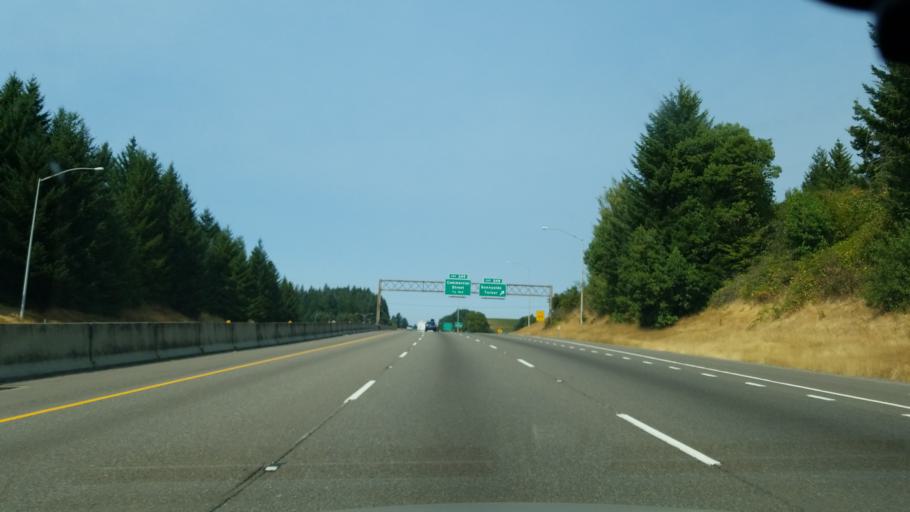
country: US
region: Oregon
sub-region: Marion County
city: Turner
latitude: 44.8391
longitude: -123.0082
